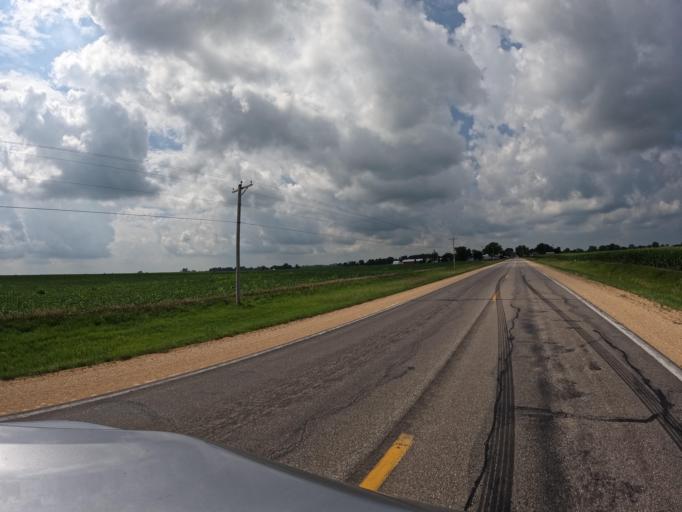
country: US
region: Iowa
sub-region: Clinton County
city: Camanche
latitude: 41.7942
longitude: -90.3549
